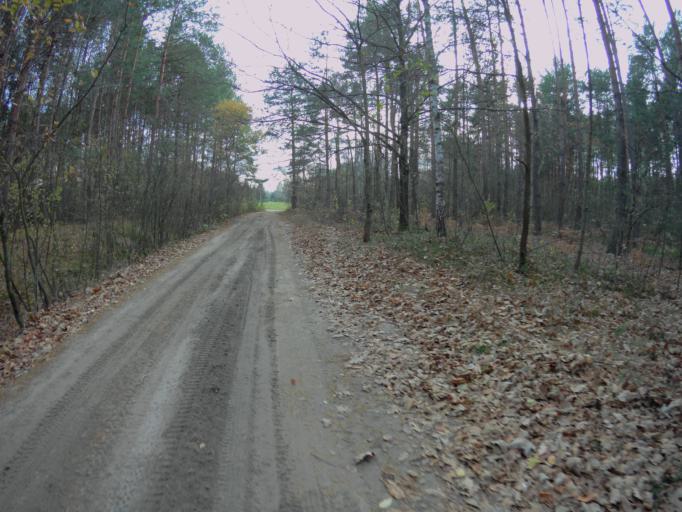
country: PL
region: Subcarpathian Voivodeship
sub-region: Powiat kolbuszowski
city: Lipnica
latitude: 50.3264
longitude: 21.9368
